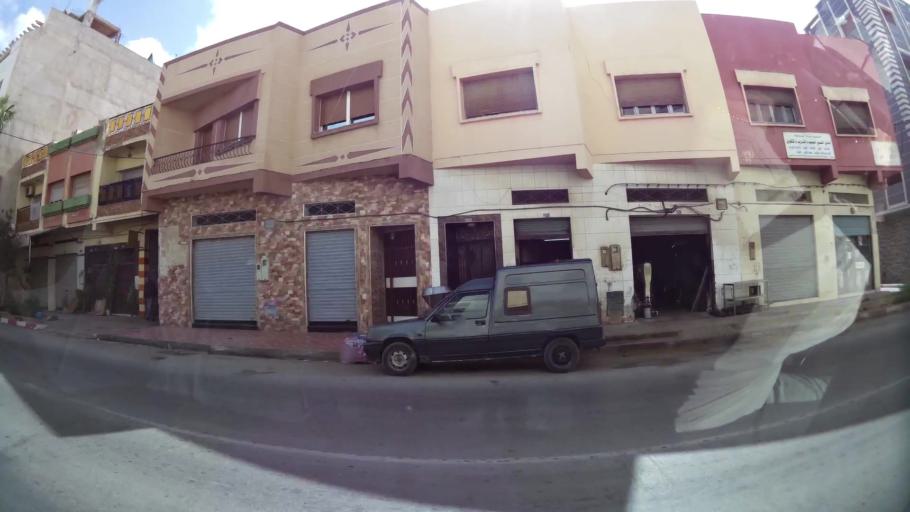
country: MA
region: Oriental
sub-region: Nador
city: Nador
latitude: 35.1652
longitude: -2.9286
